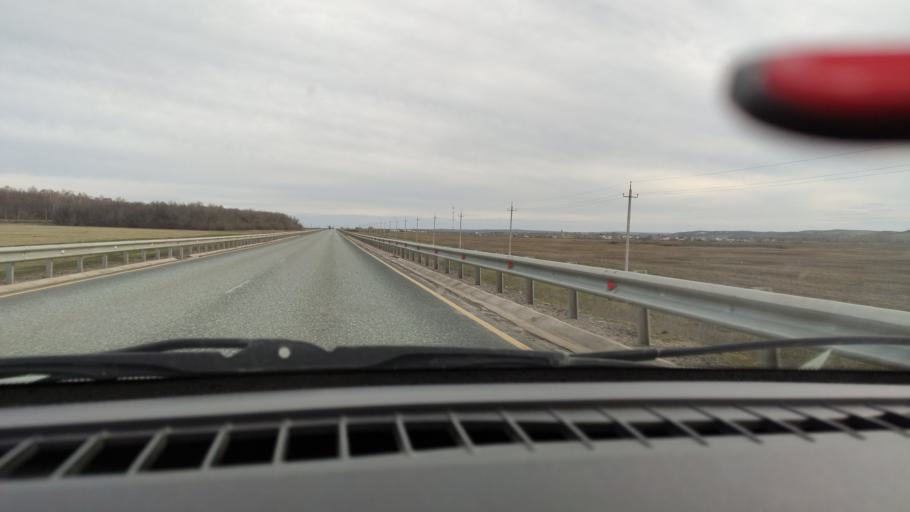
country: RU
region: Bashkortostan
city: Yermolayevo
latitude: 52.4995
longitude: 55.8295
